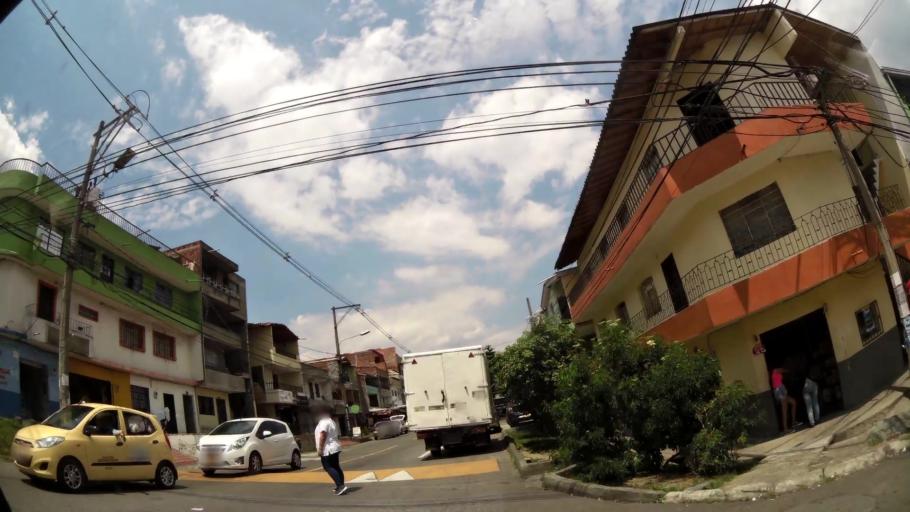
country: CO
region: Antioquia
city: Medellin
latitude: 6.2908
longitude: -75.5766
